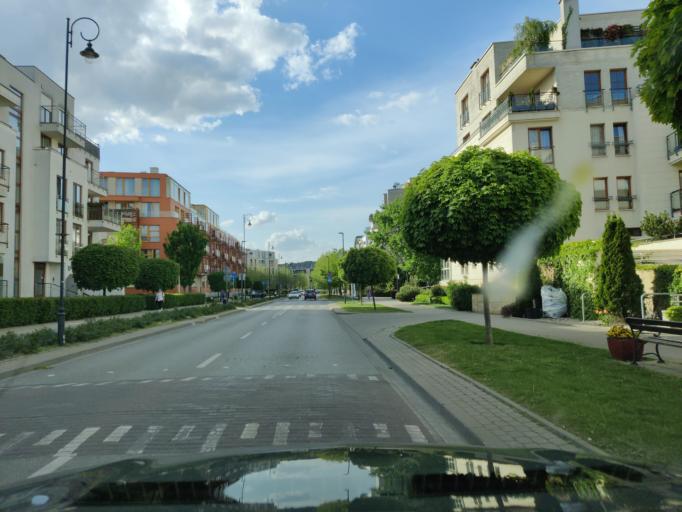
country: PL
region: Masovian Voivodeship
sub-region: Warszawa
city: Wilanow
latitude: 52.1628
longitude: 21.0760
